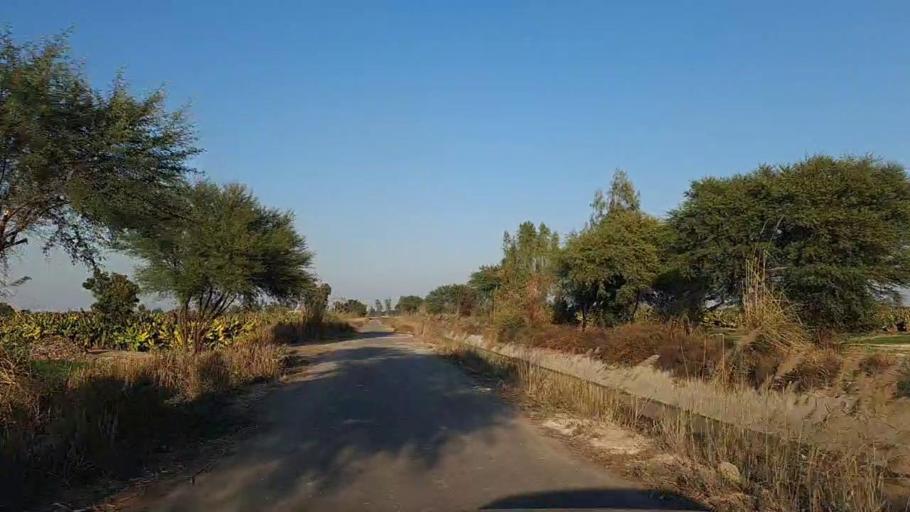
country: PK
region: Sindh
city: Sakrand
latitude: 26.2322
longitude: 68.2772
